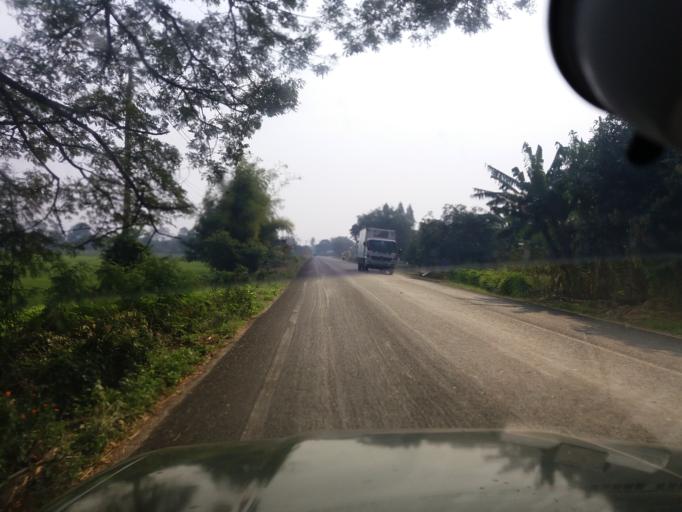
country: TH
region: Sing Buri
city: Bang Racham
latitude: 14.9106
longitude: 100.2189
